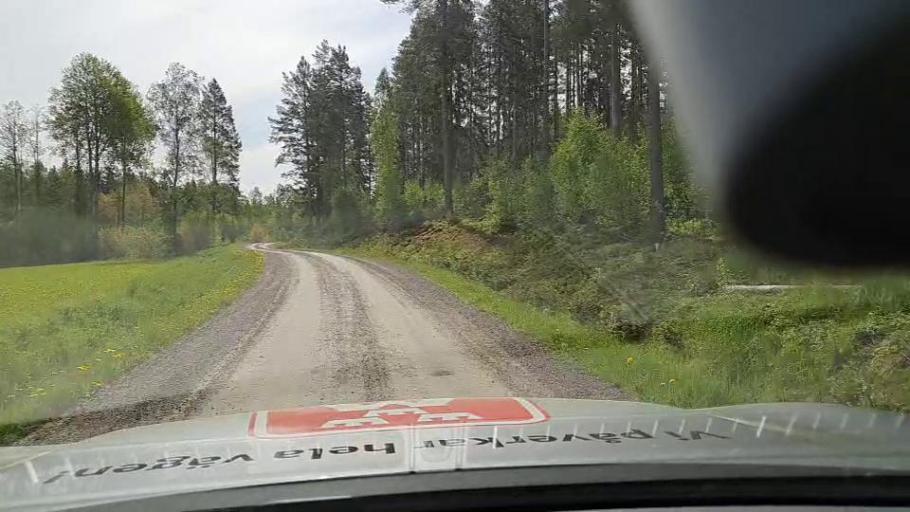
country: SE
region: Soedermanland
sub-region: Eskilstuna Kommun
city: Arla
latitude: 59.2619
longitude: 16.8239
